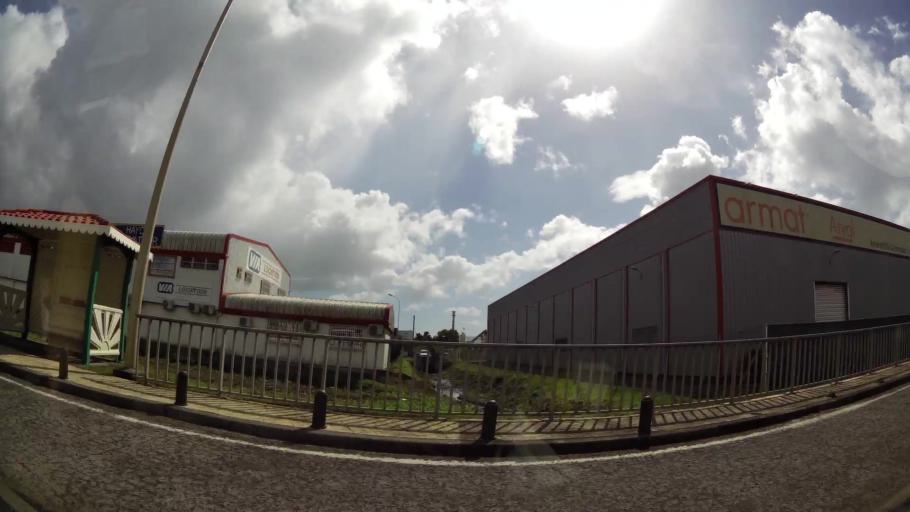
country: MQ
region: Martinique
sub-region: Martinique
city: Fort-de-France
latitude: 14.5989
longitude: -61.0473
